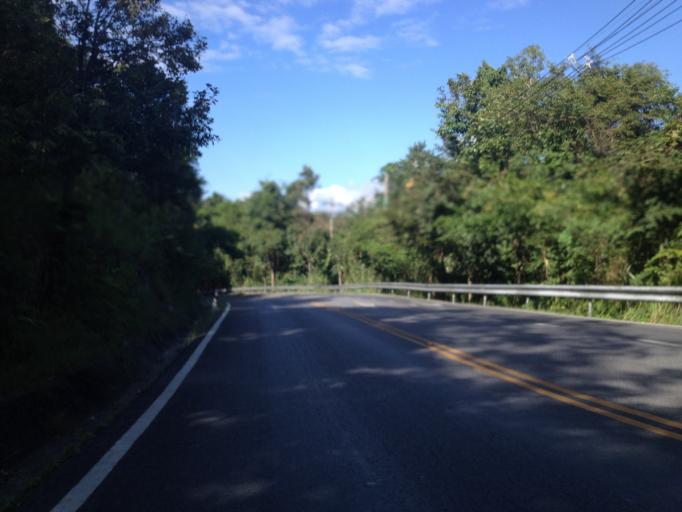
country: TH
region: Chiang Mai
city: Chiang Mai
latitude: 18.8027
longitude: 98.9347
